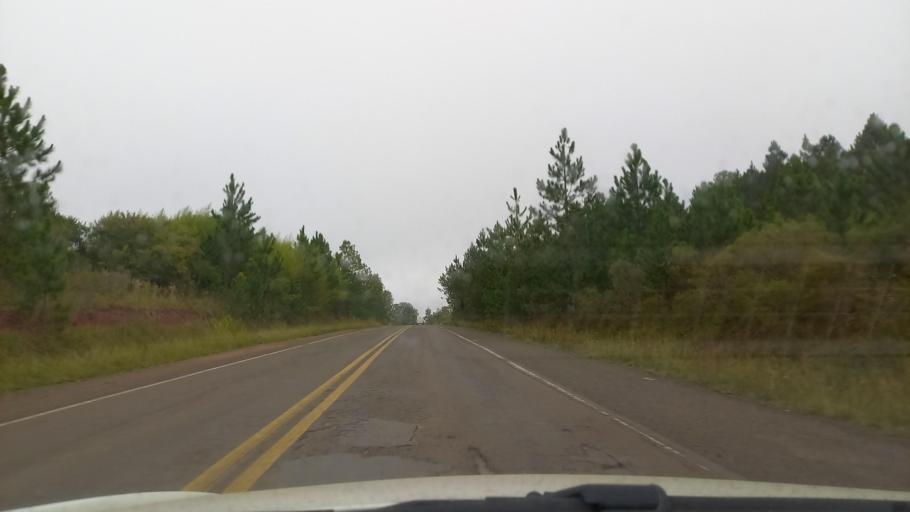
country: BR
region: Rio Grande do Sul
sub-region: Cacequi
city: Cacequi
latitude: -30.0859
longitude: -54.6251
